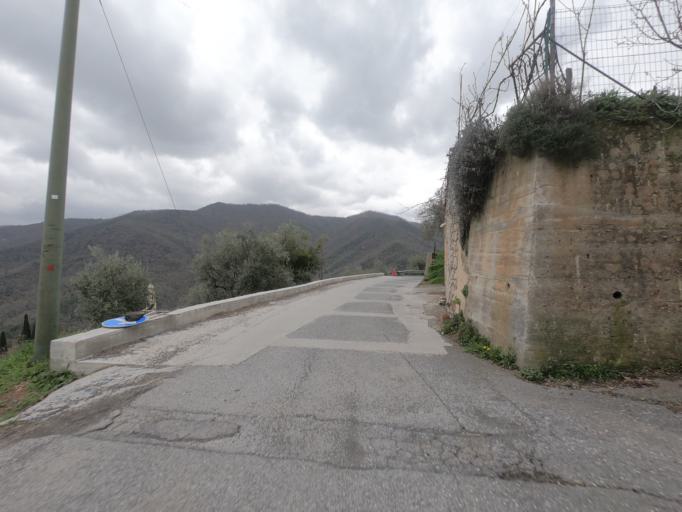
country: IT
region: Liguria
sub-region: Provincia di Savona
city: Casanova Lerrone
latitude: 44.0336
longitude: 8.0479
